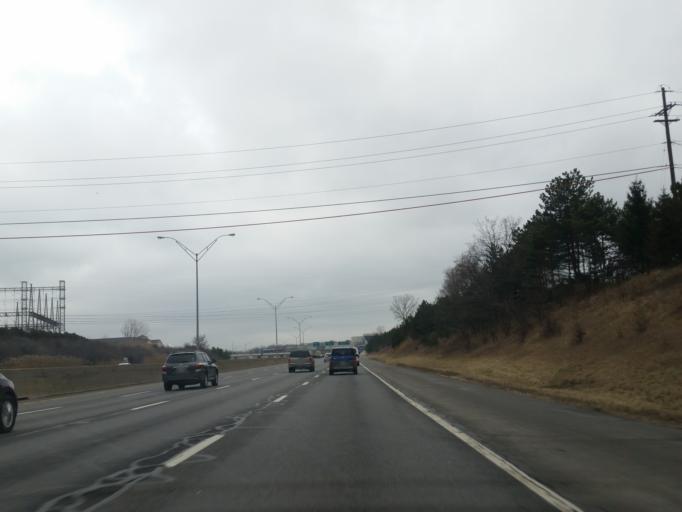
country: US
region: Ohio
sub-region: Cuyahoga County
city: Brooklyn
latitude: 41.4251
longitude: -81.7527
